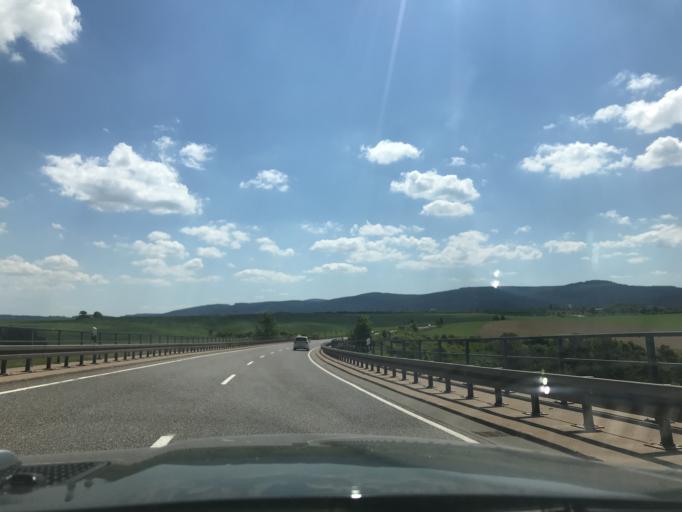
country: DE
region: Thuringia
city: Geschwenda
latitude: 50.7374
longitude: 10.8352
